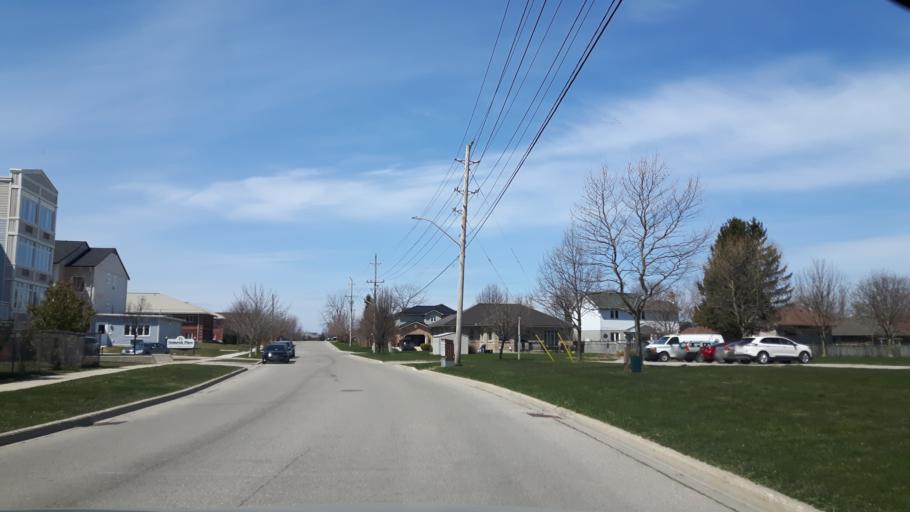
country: CA
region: Ontario
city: Goderich
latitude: 43.7290
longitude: -81.7085
